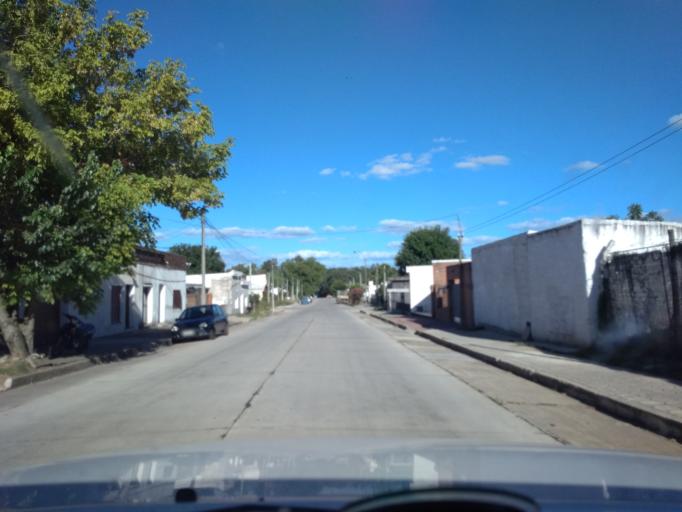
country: UY
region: Florida
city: Florida
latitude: -34.0920
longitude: -56.2122
